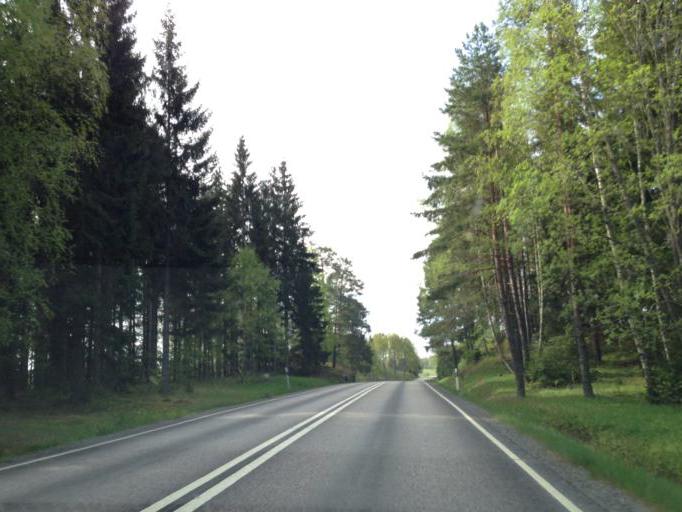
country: SE
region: Soedermanland
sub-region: Nykopings Kommun
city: Stigtomta
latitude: 58.9688
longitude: 16.8537
